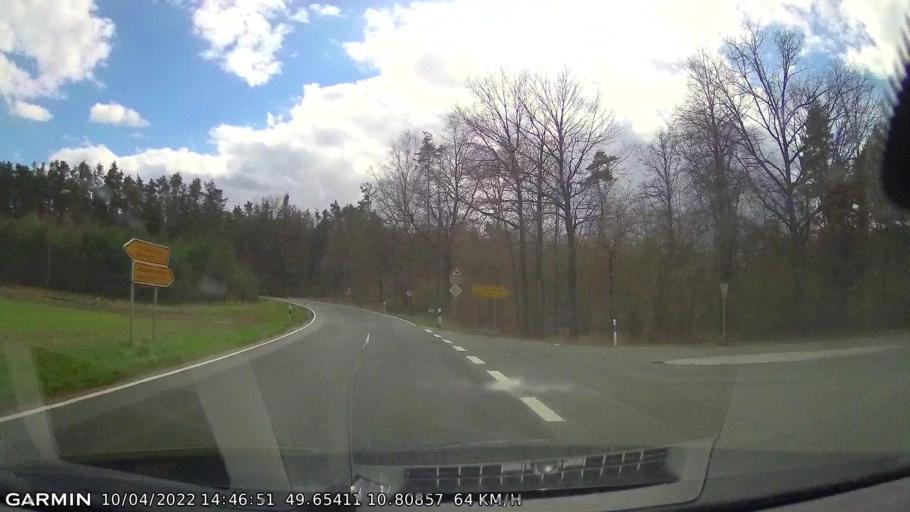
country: DE
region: Bavaria
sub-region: Regierungsbezirk Mittelfranken
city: Weisendorf
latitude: 49.6541
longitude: 10.8086
